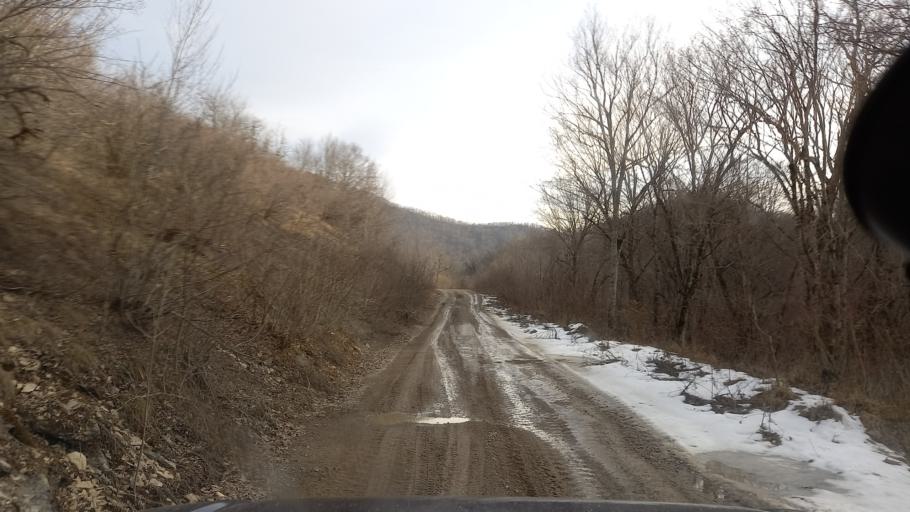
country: RU
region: Adygeya
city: Kamennomostskiy
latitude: 44.1506
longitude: 40.2967
